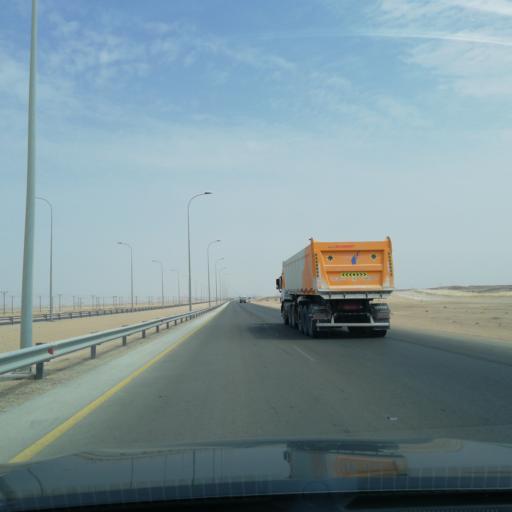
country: OM
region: Zufar
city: Salalah
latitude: 17.5672
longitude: 54.0477
